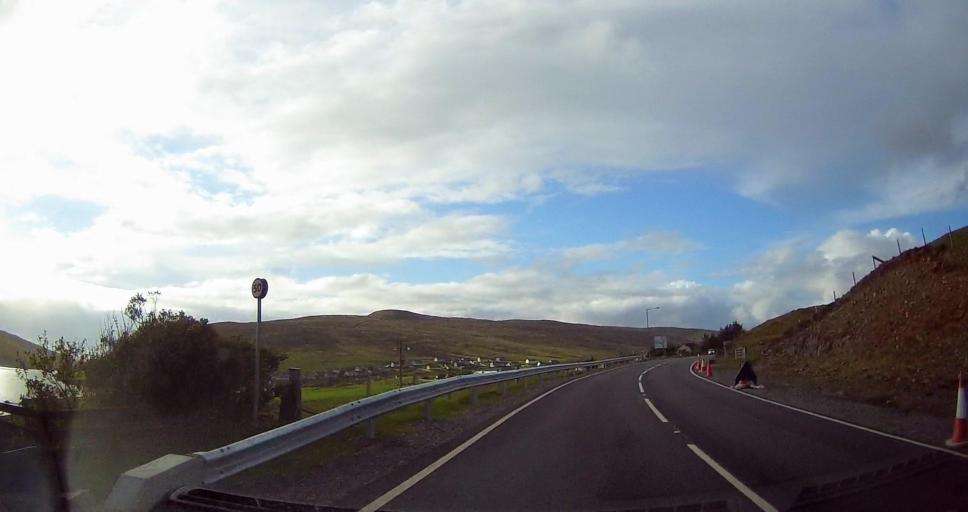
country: GB
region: Scotland
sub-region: Shetland Islands
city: Lerwick
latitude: 60.3527
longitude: -1.2611
